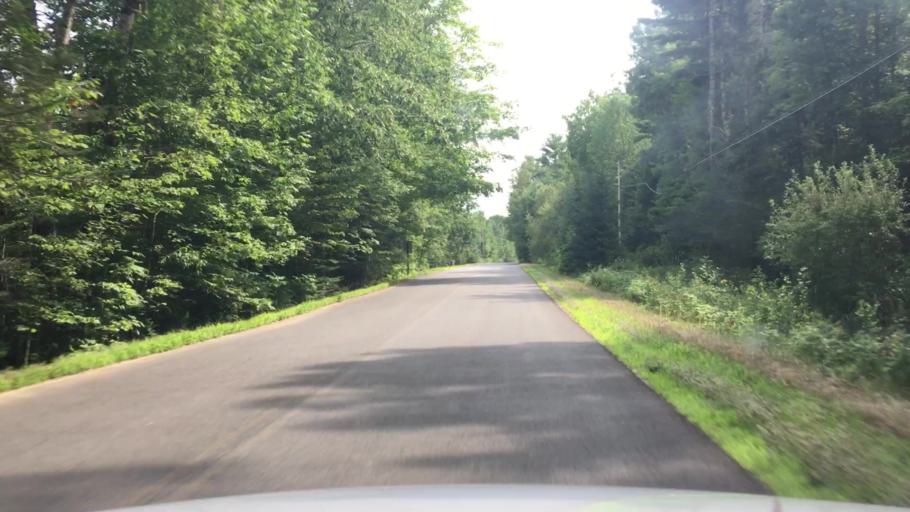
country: US
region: Maine
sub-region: Lincoln County
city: Jefferson
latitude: 44.2316
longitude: -69.4444
